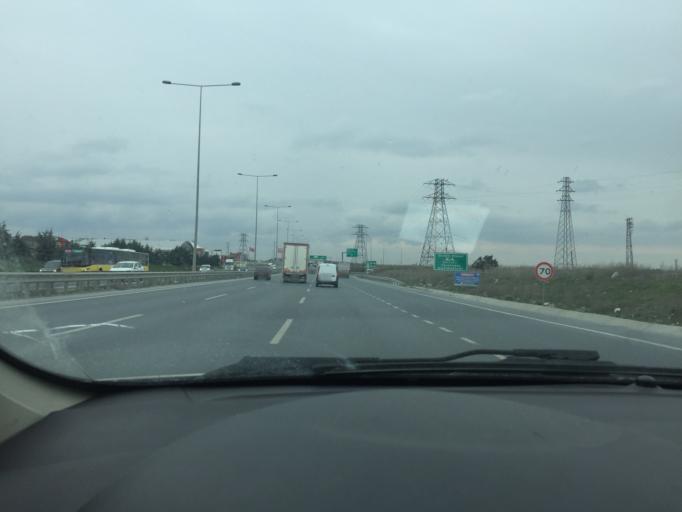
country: TR
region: Istanbul
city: Basaksehir
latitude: 41.1422
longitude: 28.8002
